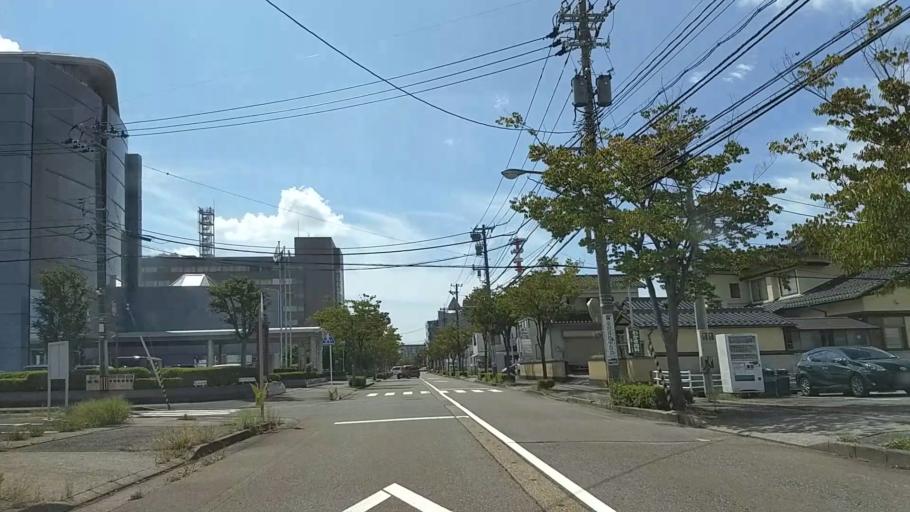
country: JP
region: Ishikawa
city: Kanazawa-shi
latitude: 36.5907
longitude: 136.6358
